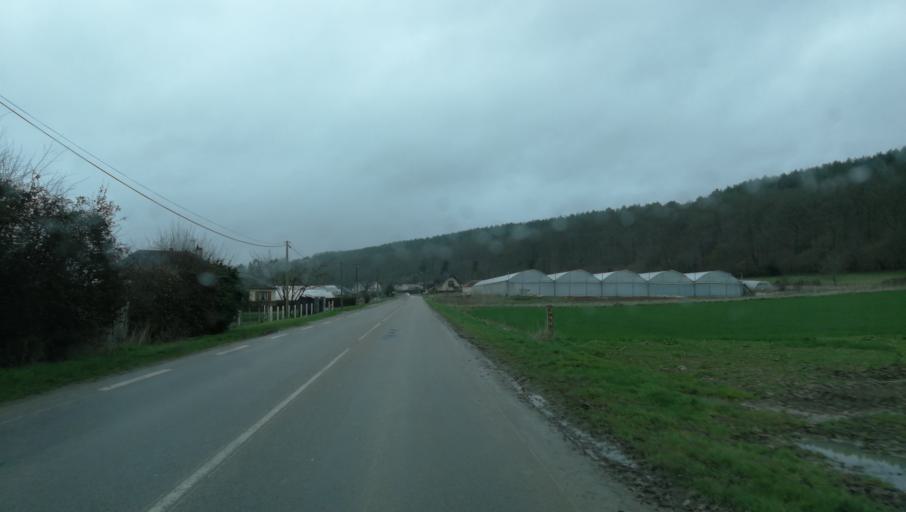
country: FR
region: Haute-Normandie
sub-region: Departement de l'Eure
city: Brionne
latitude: 49.1764
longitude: 0.7247
